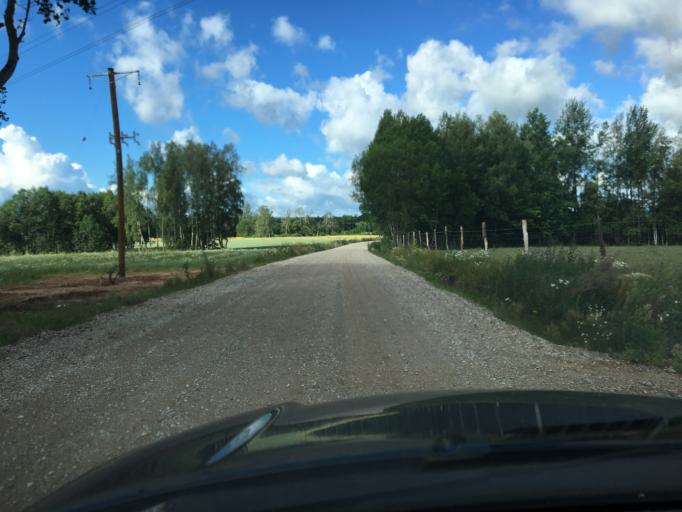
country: LV
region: Kuldigas Rajons
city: Kuldiga
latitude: 56.8388
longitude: 21.9226
